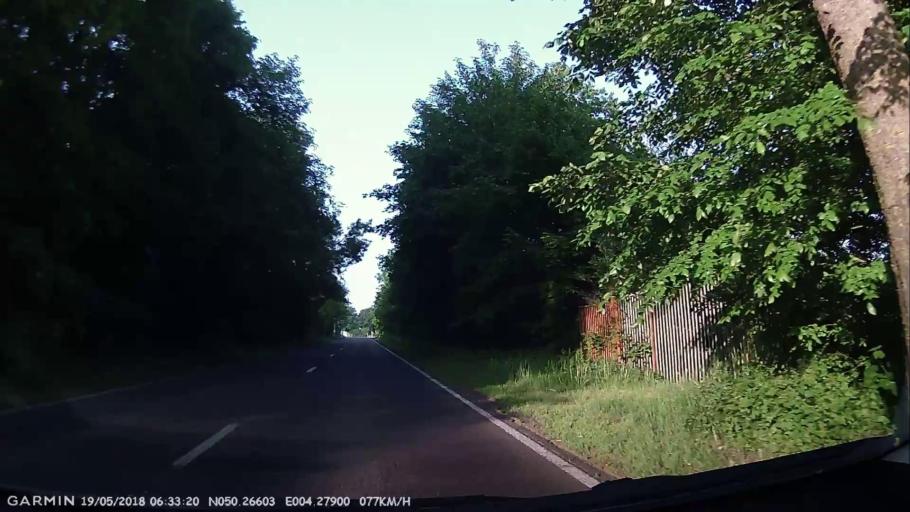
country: BE
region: Wallonia
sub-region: Province du Hainaut
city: Beaumont
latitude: 50.2660
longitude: 4.2790
